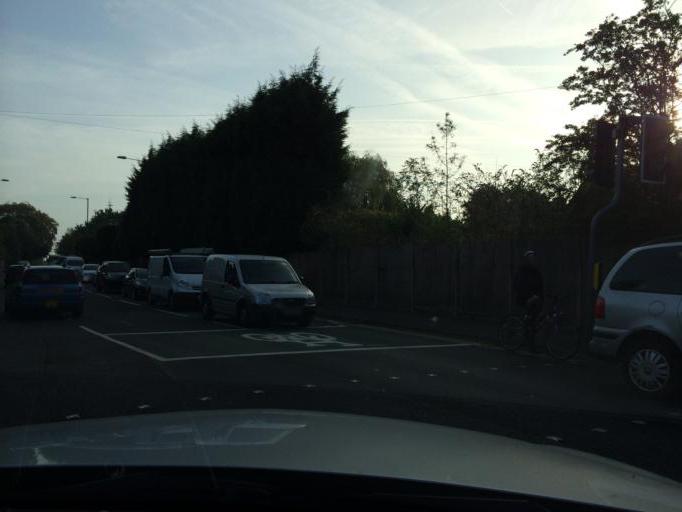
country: GB
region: England
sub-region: Borough of Stockport
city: Bramhall
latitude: 53.3815
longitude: -2.1566
